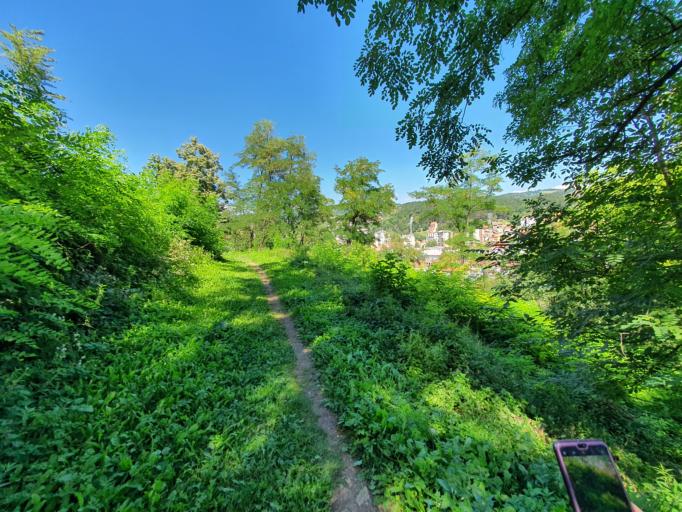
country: RS
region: Central Serbia
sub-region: Zlatiborski Okrug
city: Uzice
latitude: 43.8503
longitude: 19.8434
